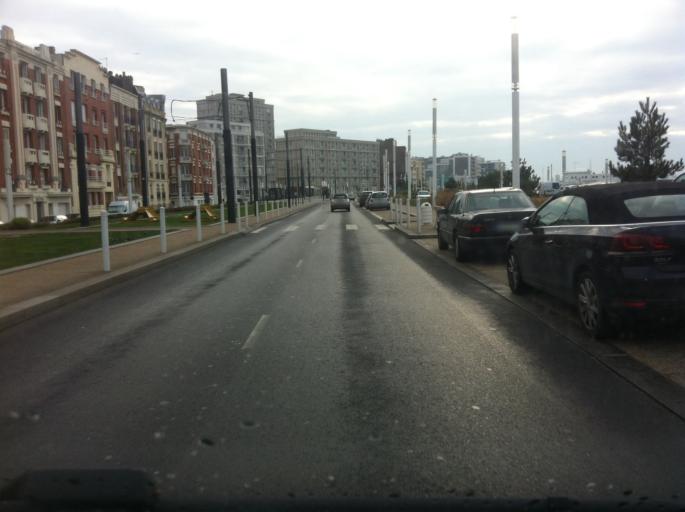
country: FR
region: Haute-Normandie
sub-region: Departement de la Seine-Maritime
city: Le Havre
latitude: 49.4951
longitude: 0.0945
